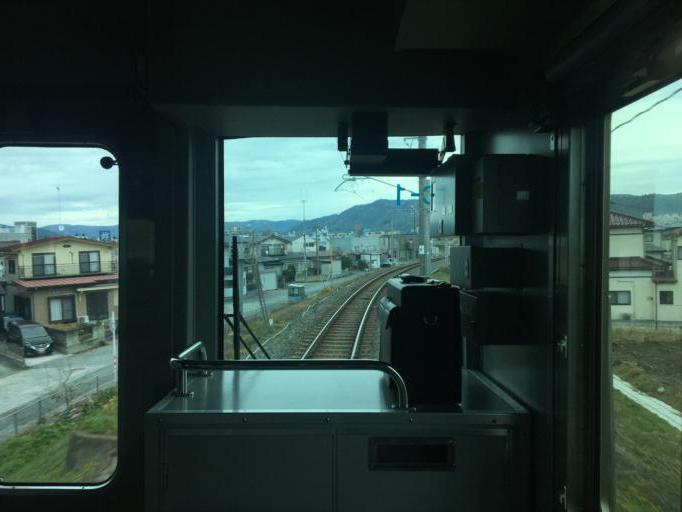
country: JP
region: Miyagi
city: Ishinomaki
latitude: 38.4379
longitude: 141.2939
